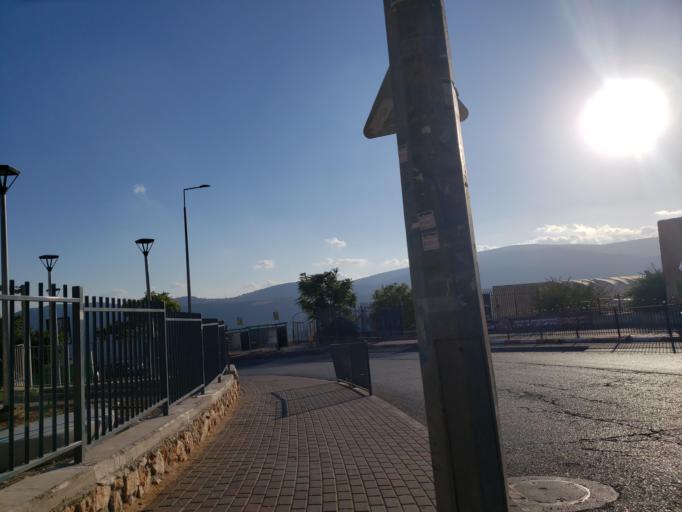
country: IL
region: Northern District
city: Safed
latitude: 32.9663
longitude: 35.4872
